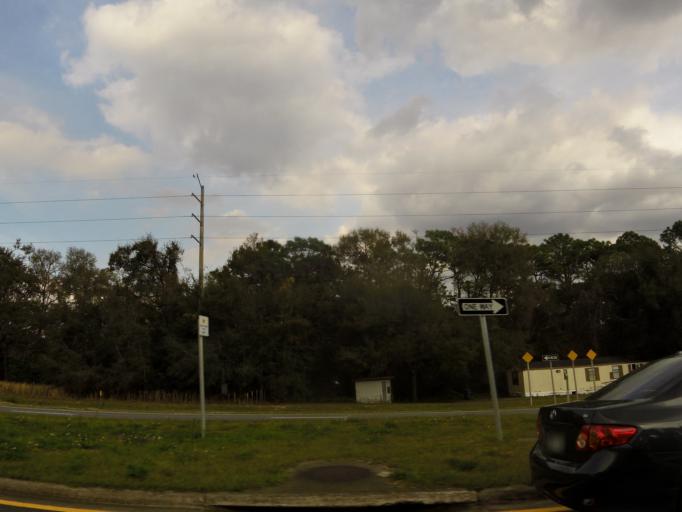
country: US
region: Florida
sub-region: Volusia County
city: De Leon Springs
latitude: 29.0897
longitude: -81.3279
